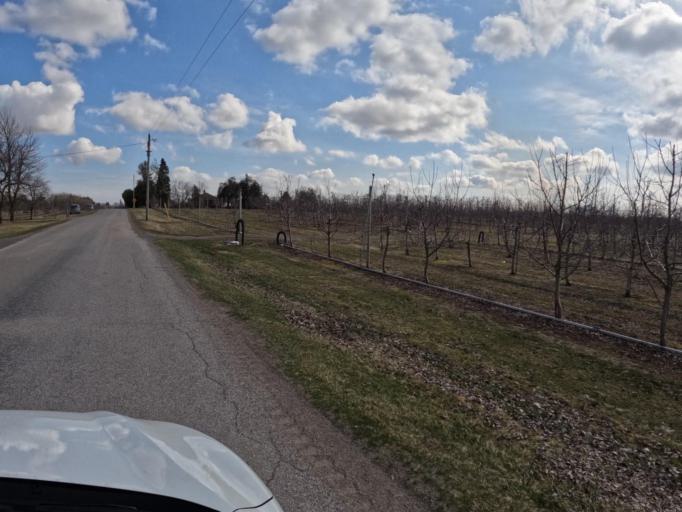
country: CA
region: Ontario
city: Norfolk County
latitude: 42.8789
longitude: -80.2812
